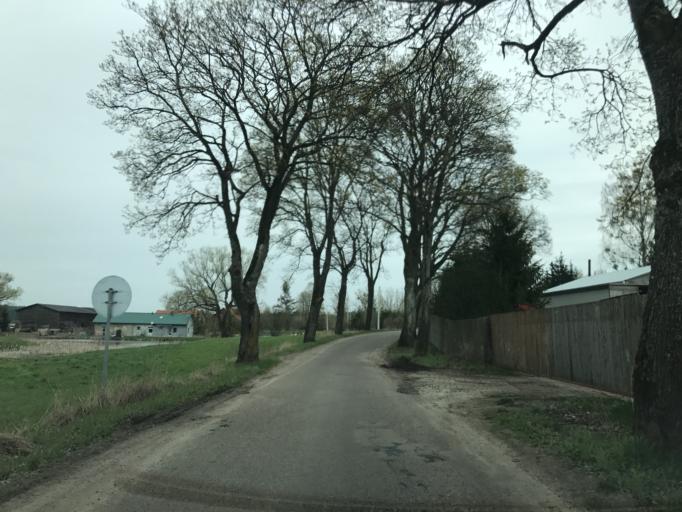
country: PL
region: Warmian-Masurian Voivodeship
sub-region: Powiat olsztynski
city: Olsztynek
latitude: 53.6153
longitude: 20.2468
